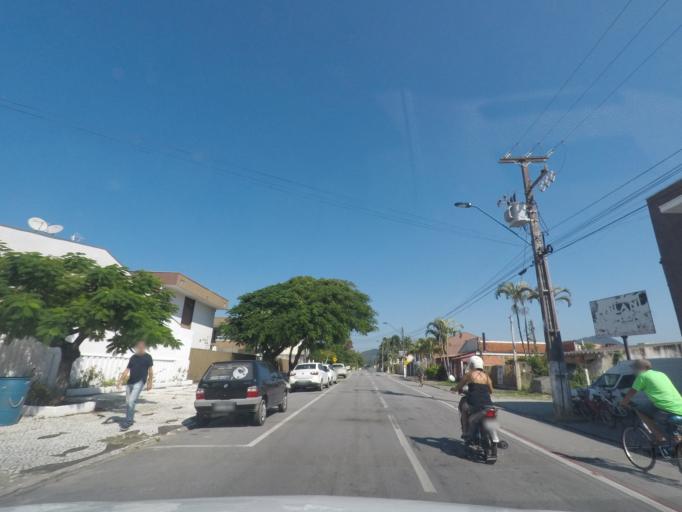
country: BR
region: Parana
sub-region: Guaratuba
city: Guaratuba
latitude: -25.8218
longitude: -48.5351
